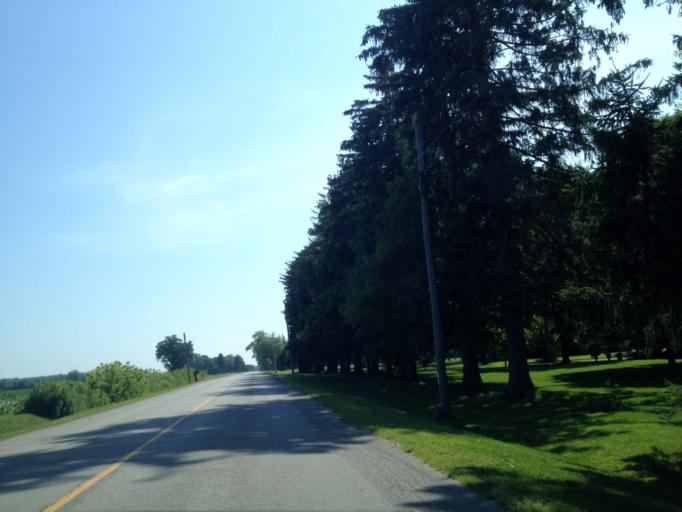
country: CA
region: Ontario
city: London
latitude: 43.1229
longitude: -81.2319
